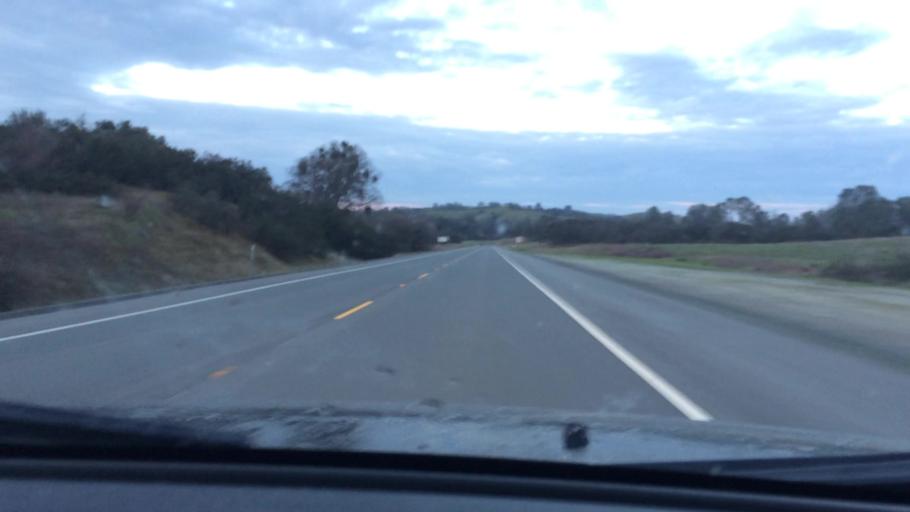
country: US
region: California
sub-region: Amador County
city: Ione
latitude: 38.3945
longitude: -120.9001
